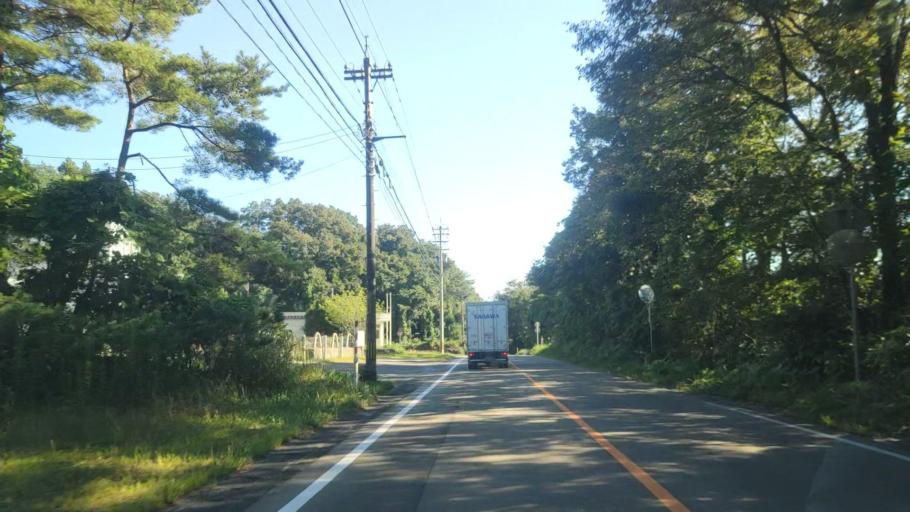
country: JP
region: Ishikawa
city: Nanao
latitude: 37.2103
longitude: 136.9080
